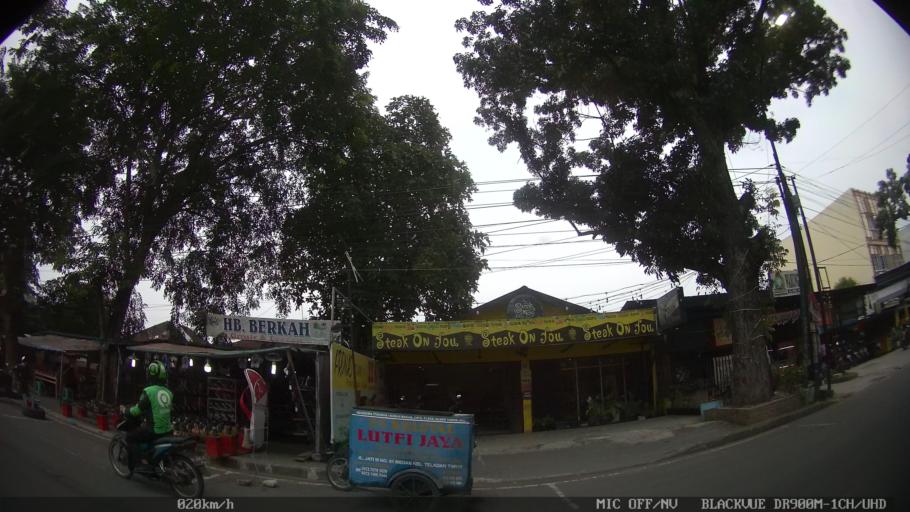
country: ID
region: North Sumatra
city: Medan
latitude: 3.5685
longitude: 98.6973
